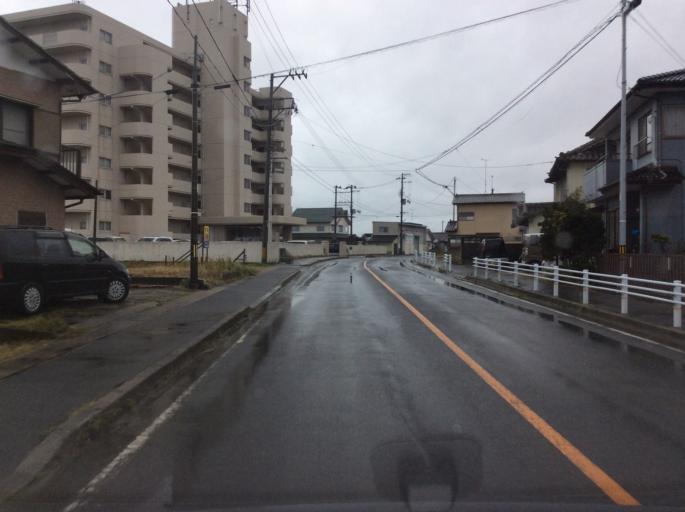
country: JP
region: Fukushima
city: Iwaki
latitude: 37.1019
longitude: 140.9874
